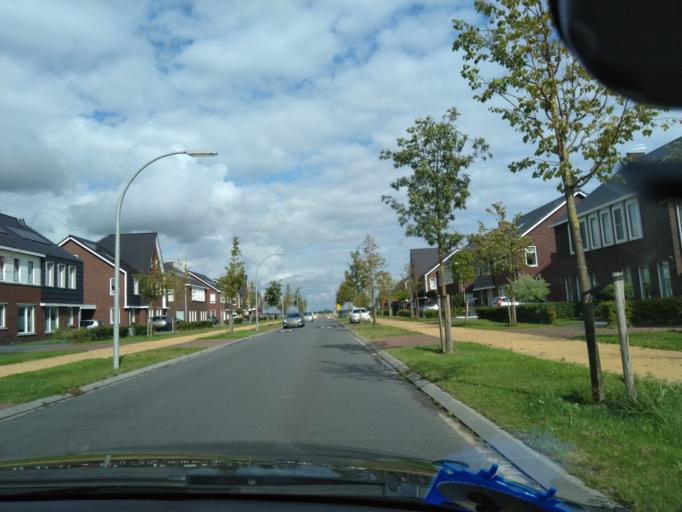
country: NL
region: Groningen
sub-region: Gemeente Zuidhorn
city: Zuidhorn
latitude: 53.2503
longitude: 6.4141
